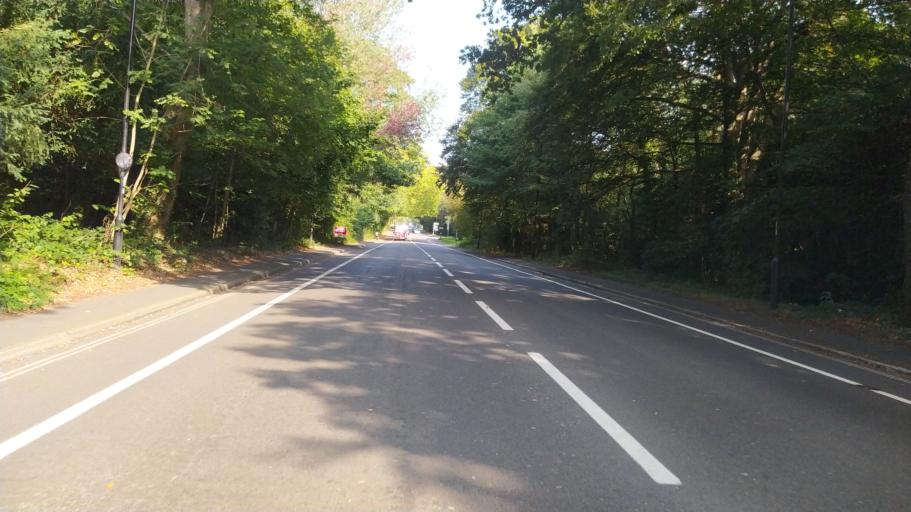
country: GB
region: England
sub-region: Southampton
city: Southampton
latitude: 50.9329
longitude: -1.4062
